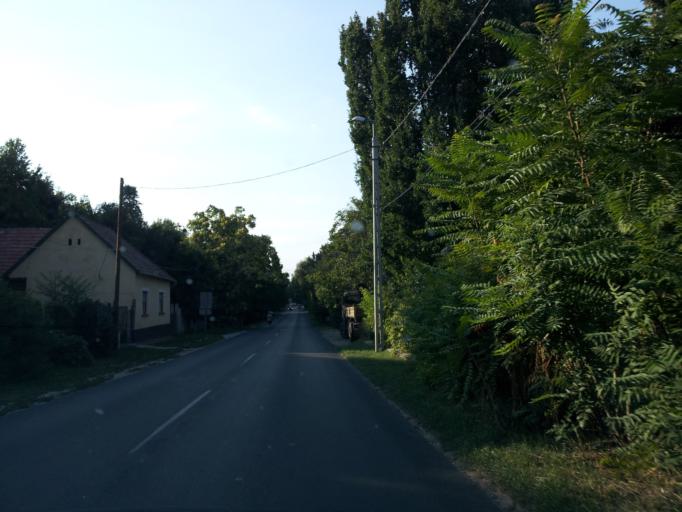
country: HU
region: Pest
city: Tahitotfalu
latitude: 47.7550
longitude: 19.0748
